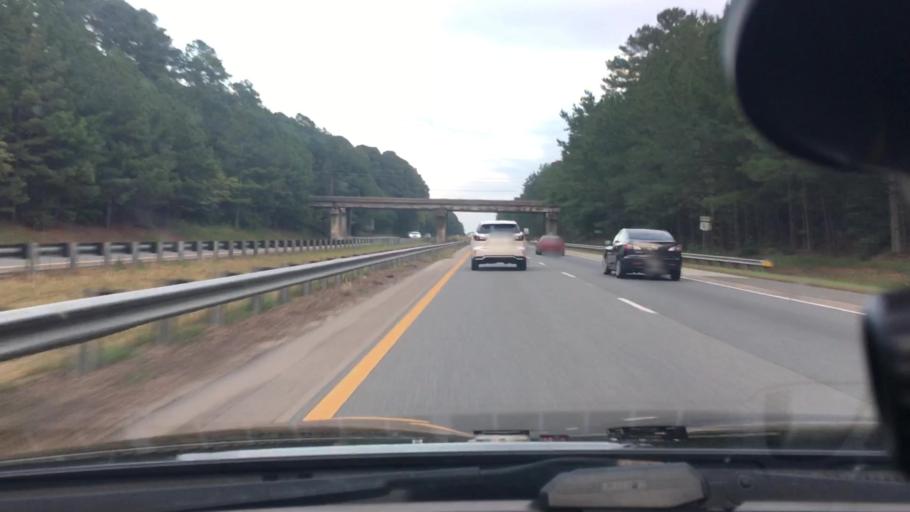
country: US
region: North Carolina
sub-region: Chatham County
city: Pittsboro
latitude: 35.6273
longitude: -79.0793
